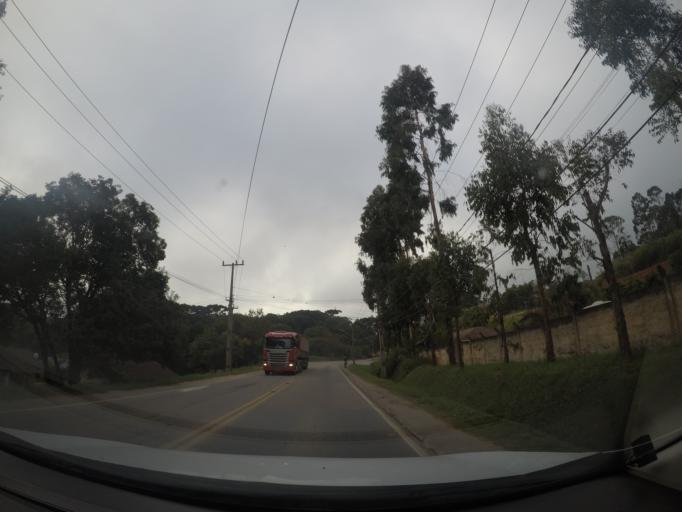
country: BR
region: Parana
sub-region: Colombo
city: Colombo
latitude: -25.2956
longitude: -49.2372
